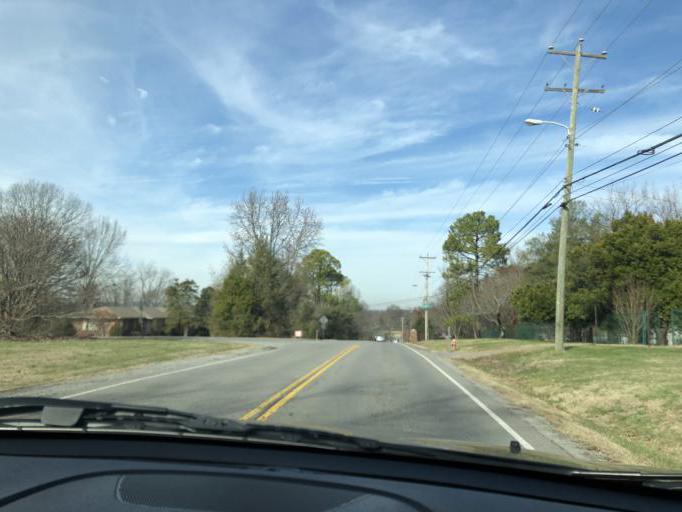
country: US
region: Tennessee
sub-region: Davidson County
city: Lakewood
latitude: 36.1992
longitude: -86.6756
